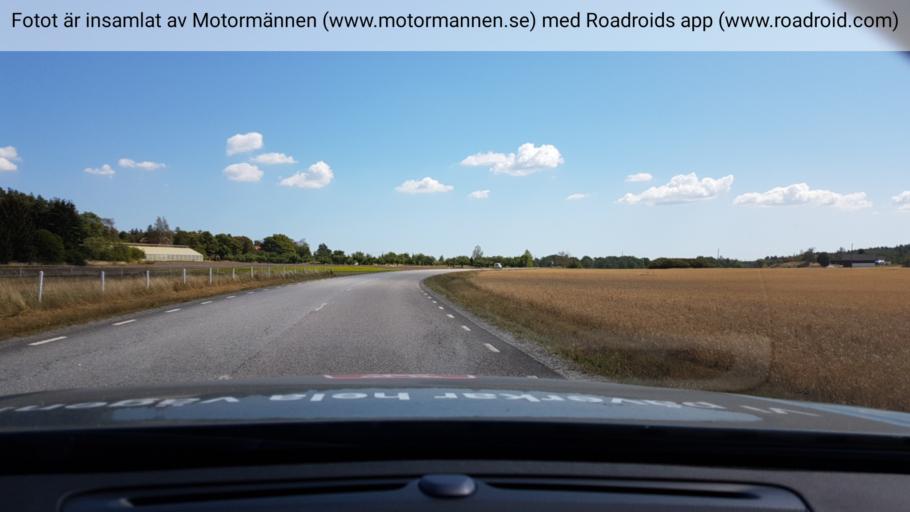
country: SE
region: Stockholm
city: Stenhamra
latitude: 59.3902
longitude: 17.6684
